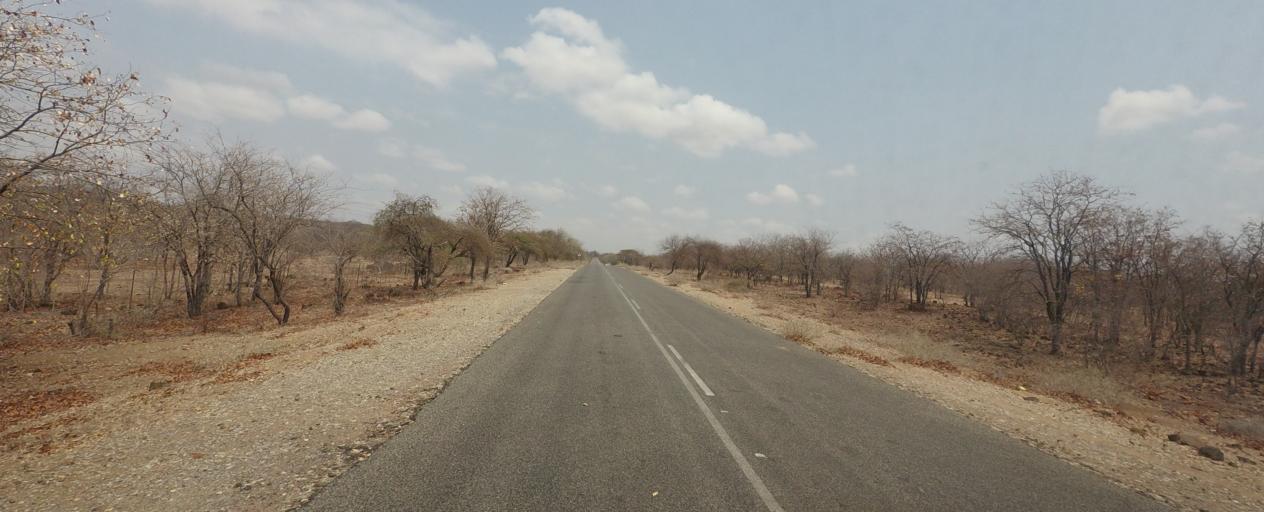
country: ZA
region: Limpopo
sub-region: Vhembe District Municipality
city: Mutale
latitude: -22.4208
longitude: 30.9540
